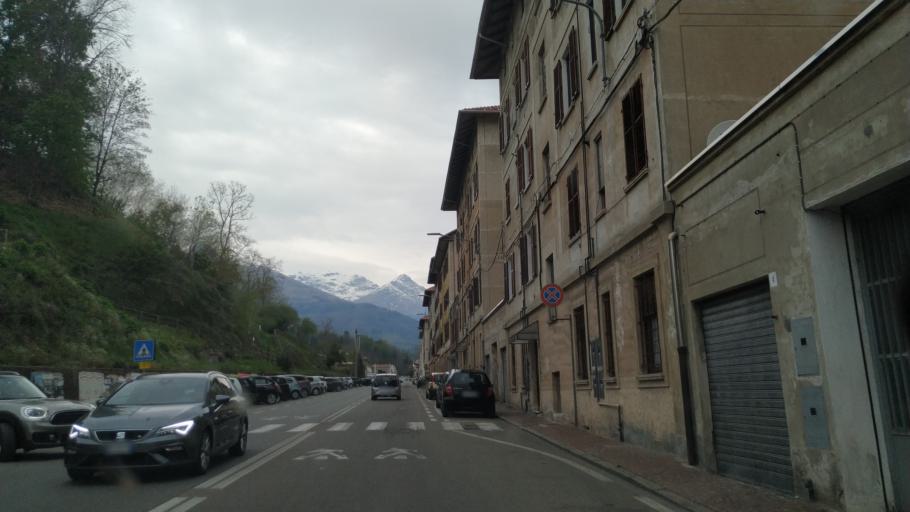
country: IT
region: Piedmont
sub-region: Provincia di Biella
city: Occhieppo Inferiore
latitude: 45.5565
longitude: 8.0284
